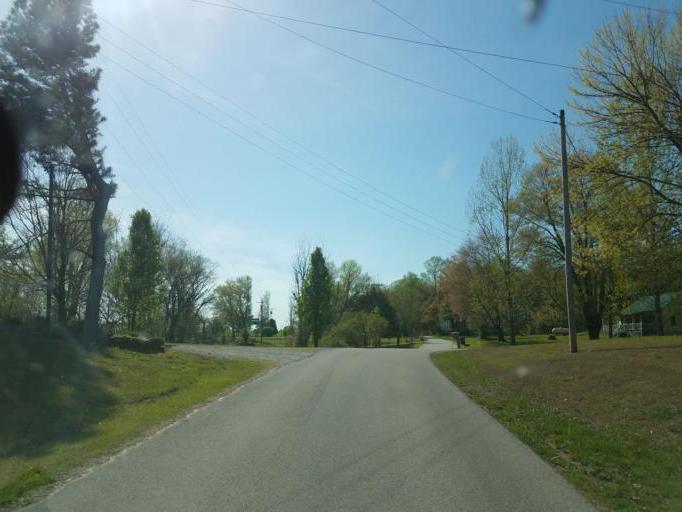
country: US
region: Kentucky
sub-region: Edmonson County
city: Brownsville
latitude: 37.1218
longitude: -86.1397
